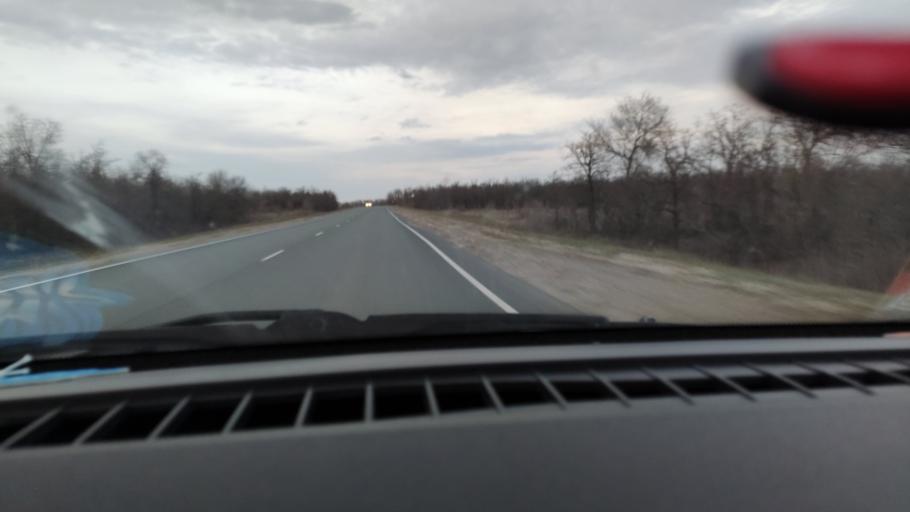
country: RU
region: Saratov
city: Sinodskoye
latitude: 51.9353
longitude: 46.5901
